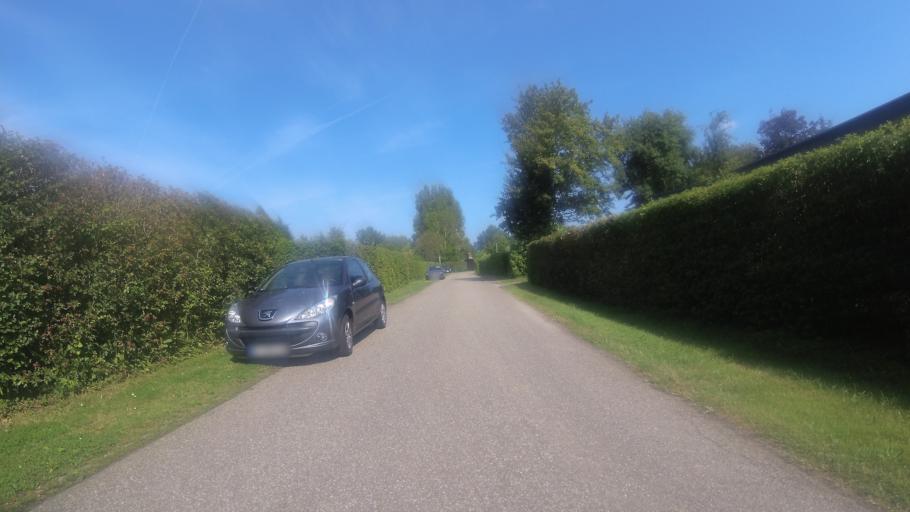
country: NL
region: Zeeland
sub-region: Gemeente Noord-Beveland
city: Kamperland
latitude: 51.5595
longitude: 3.6902
